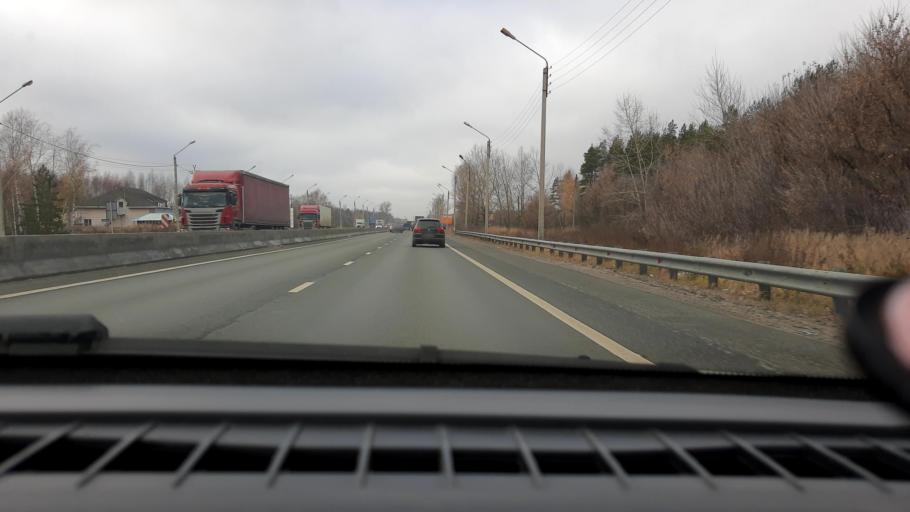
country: RU
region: Nizjnij Novgorod
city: Gorbatovka
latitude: 56.3079
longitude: 43.7029
